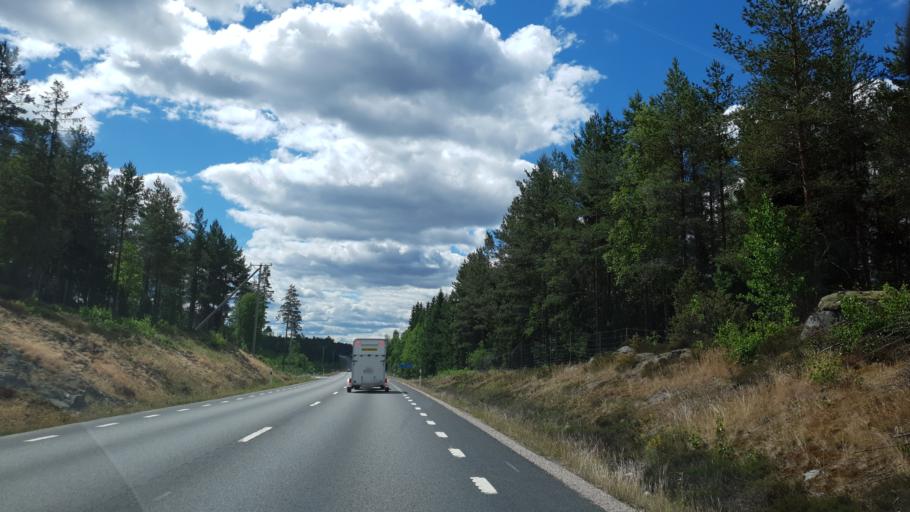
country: SE
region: Kronoberg
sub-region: Vaxjo Kommun
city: Braas
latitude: 57.1923
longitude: 15.1562
